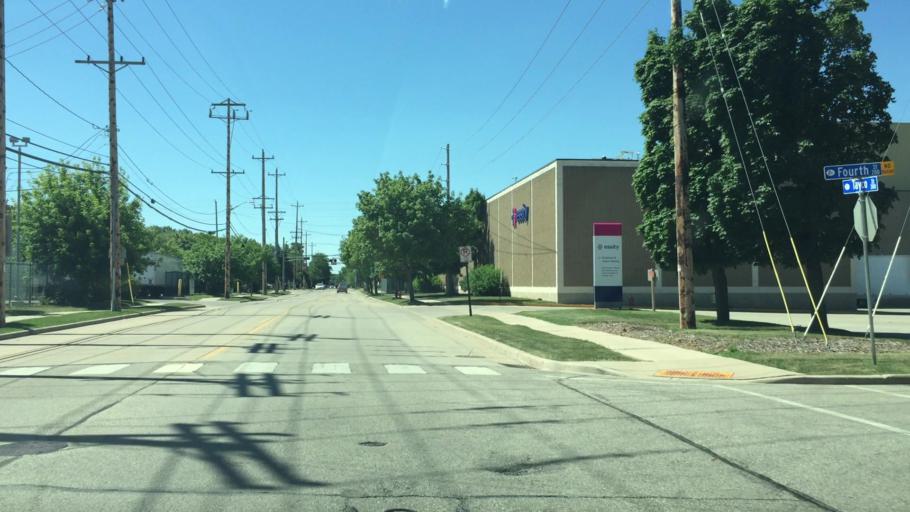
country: US
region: Wisconsin
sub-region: Winnebago County
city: Menasha
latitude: 44.2066
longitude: -88.4532
